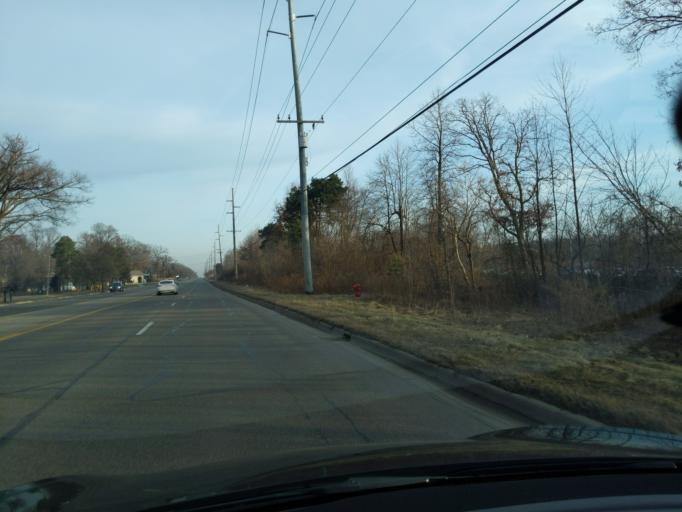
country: US
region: Michigan
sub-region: Livingston County
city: Howell
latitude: 42.5791
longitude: -83.8523
